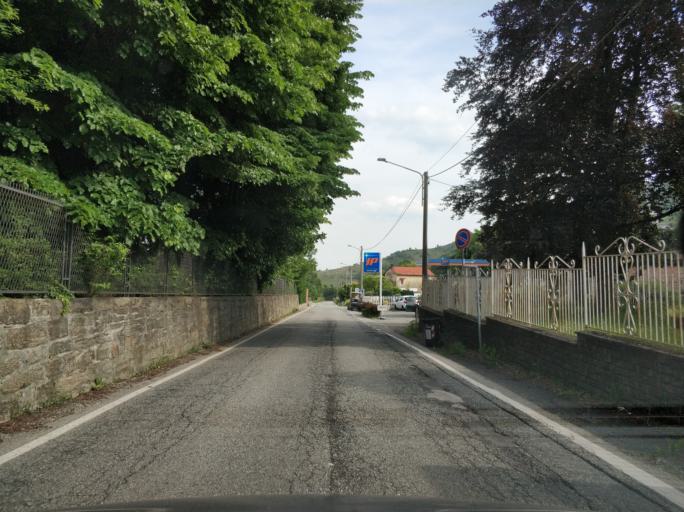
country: IT
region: Piedmont
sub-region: Provincia di Torino
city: Corio
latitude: 45.3091
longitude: 7.5365
